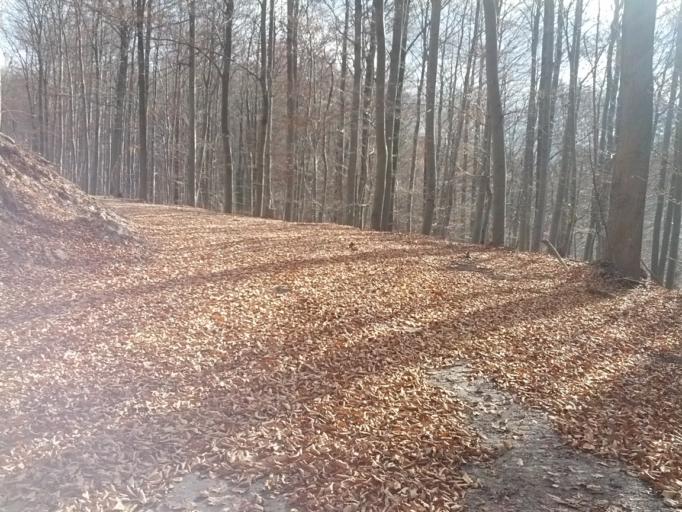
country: DE
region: Thuringia
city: Krauthausen
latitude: 50.9782
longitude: 10.2320
